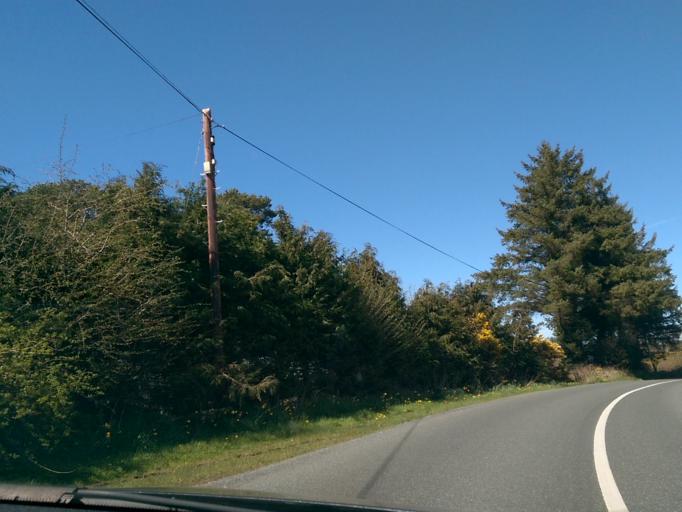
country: IE
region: Leinster
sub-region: Wicklow
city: Carnew
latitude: 52.8276
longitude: -6.5225
